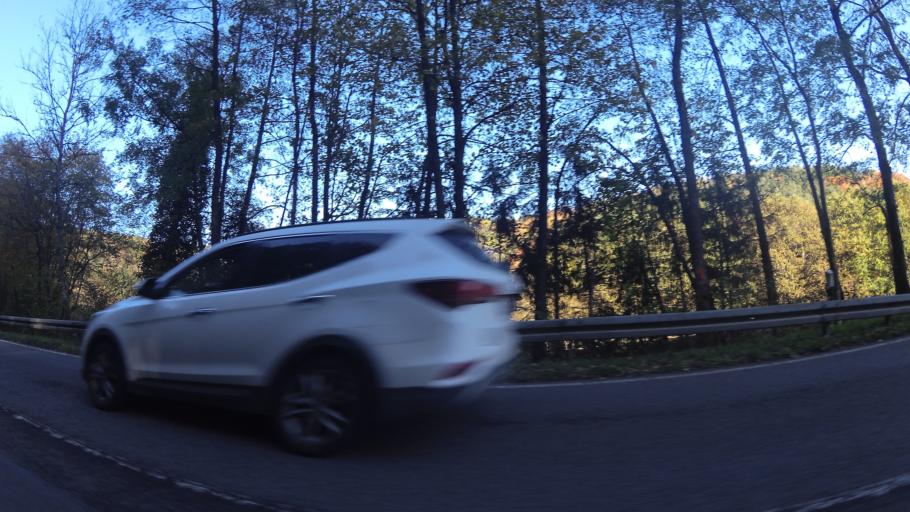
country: DE
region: Saarland
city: Losheim
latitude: 49.4699
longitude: 6.7497
